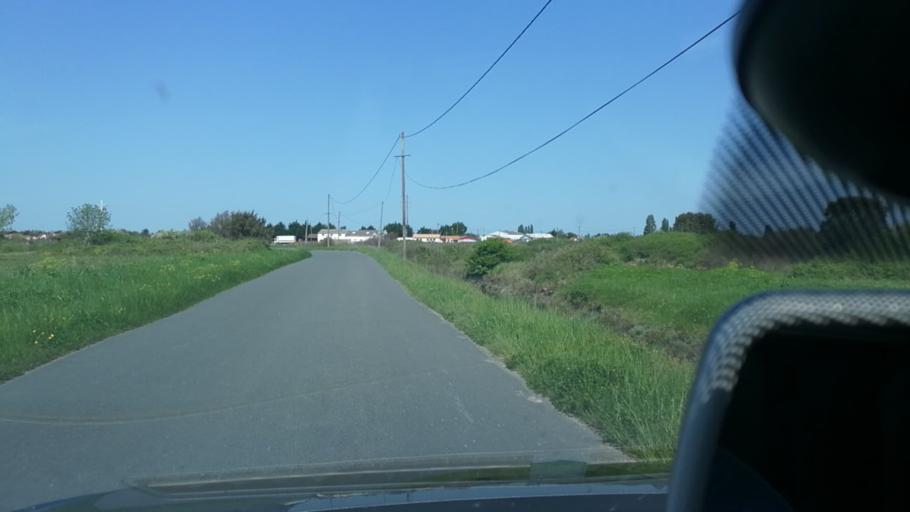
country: FR
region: Poitou-Charentes
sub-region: Departement de la Charente-Maritime
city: Saint-Trojan-les-Bains
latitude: 45.8678
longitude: -1.2203
